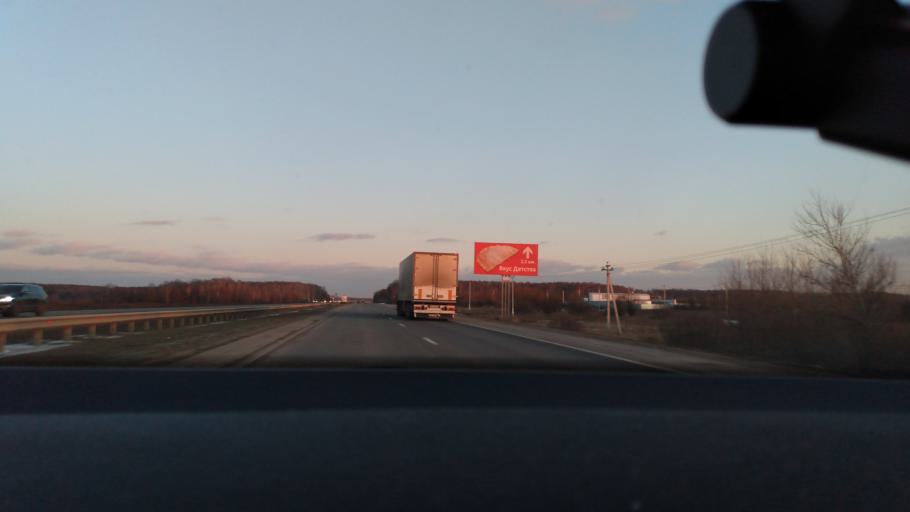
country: RU
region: Moskovskaya
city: Kolomna
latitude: 55.1108
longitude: 38.8687
